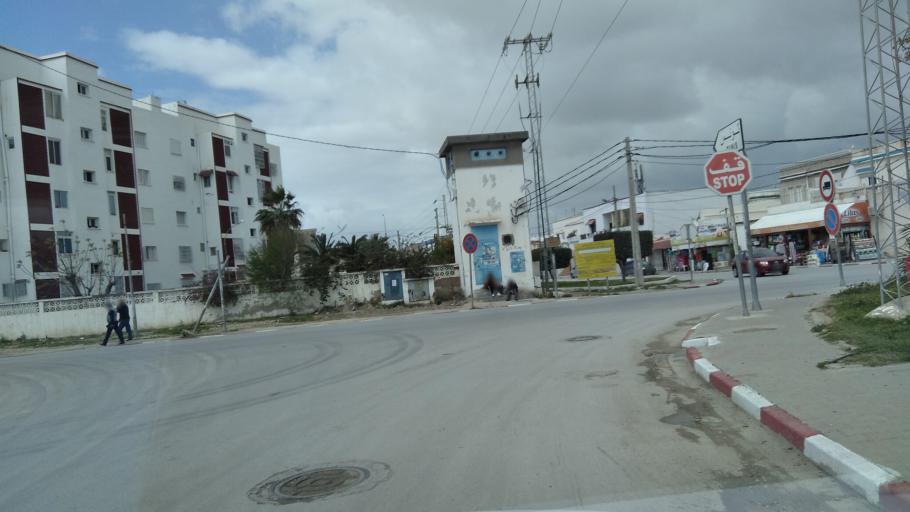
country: TN
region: Bin 'Arus
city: Ben Arous
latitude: 36.7442
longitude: 10.2263
